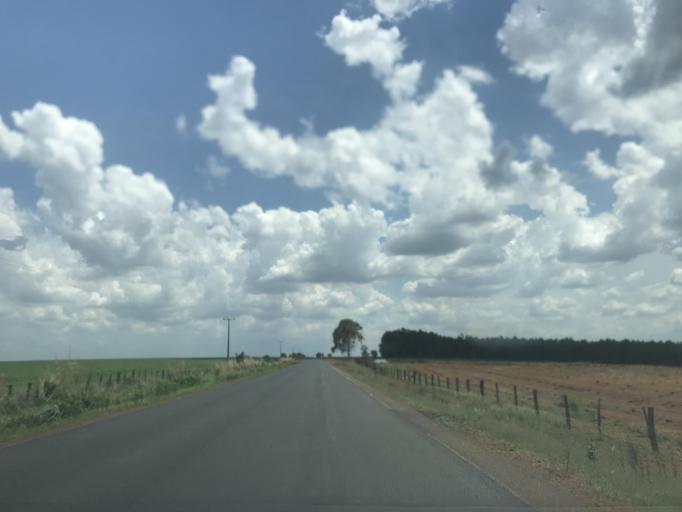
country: BR
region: Goias
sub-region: Piracanjuba
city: Piracanjuba
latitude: -17.3646
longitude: -48.7962
